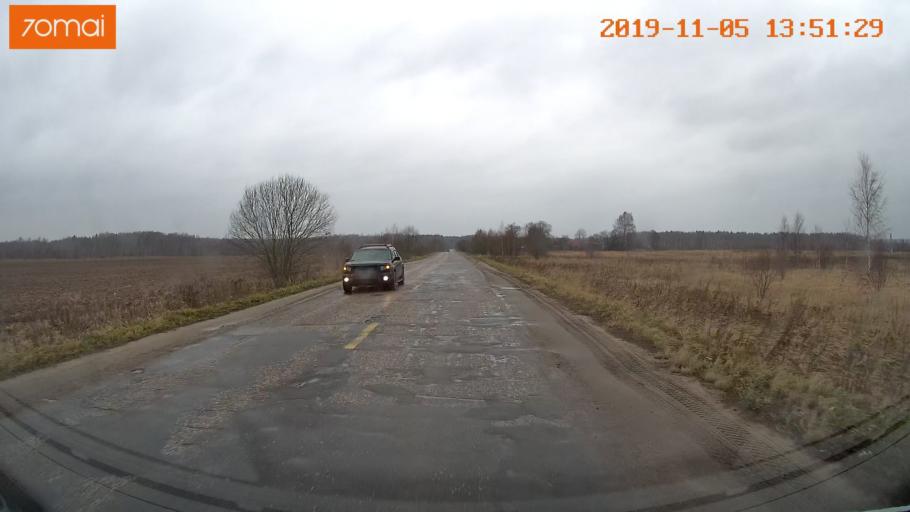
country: RU
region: Ivanovo
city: Kaminskiy
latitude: 57.0250
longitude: 41.4000
